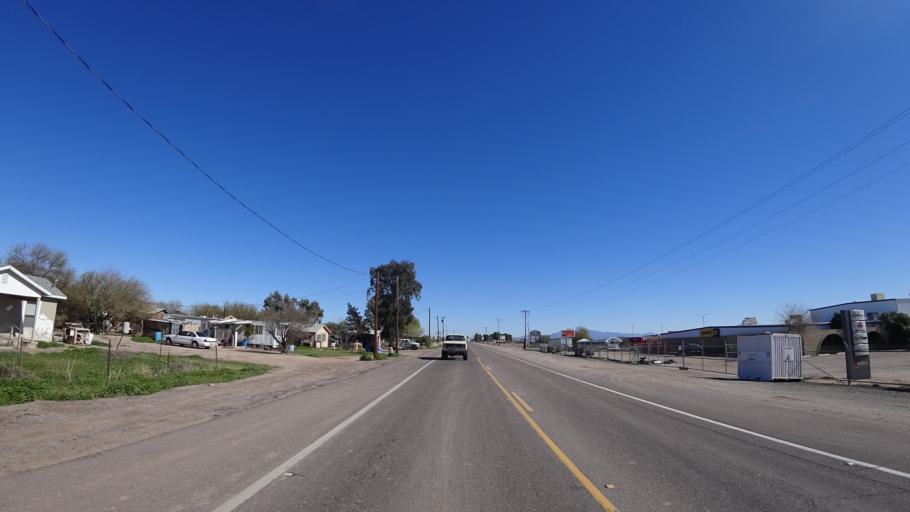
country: US
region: Arizona
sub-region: Maricopa County
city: Buckeye
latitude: 33.3703
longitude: -112.6192
